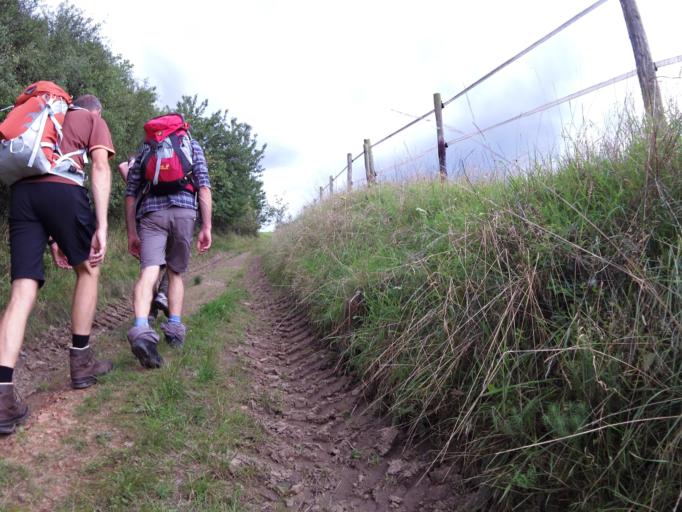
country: DE
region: Rheinland-Pfalz
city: Staudernheim
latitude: 49.7702
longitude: 7.6903
